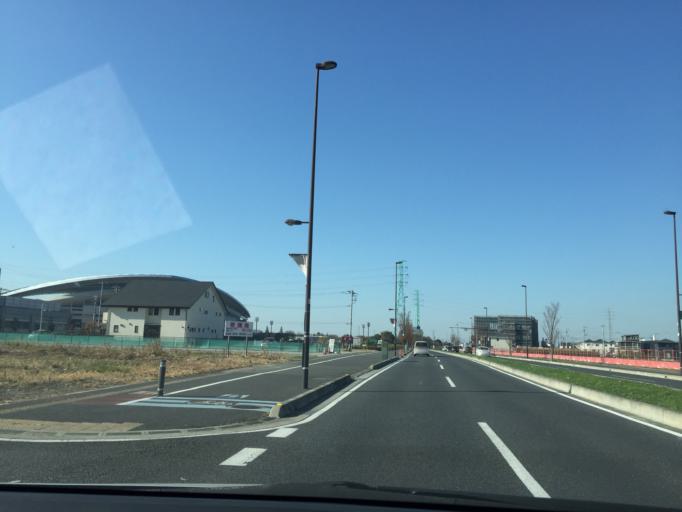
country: JP
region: Saitama
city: Koshigaya
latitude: 35.9017
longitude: 139.7244
